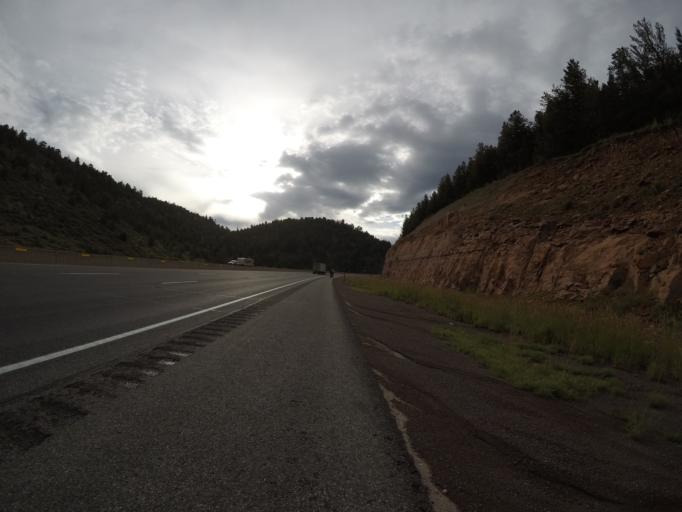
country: US
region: Wyoming
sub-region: Albany County
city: Laramie
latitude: 41.2654
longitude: -105.4704
